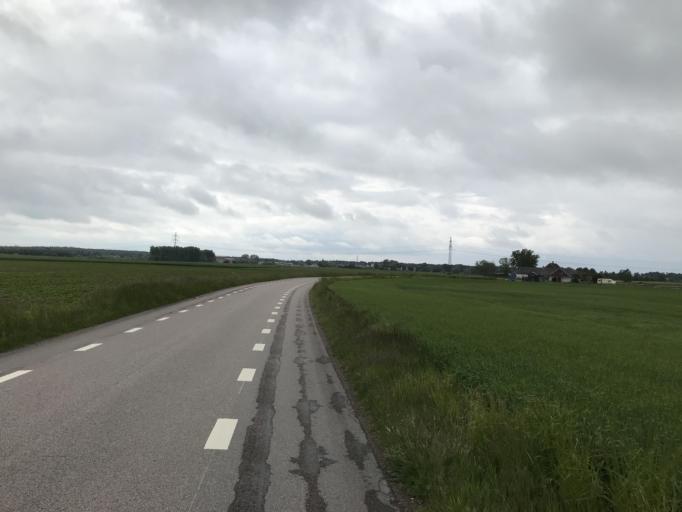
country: SE
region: Skane
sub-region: Landskrona
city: Asmundtorp
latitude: 55.8663
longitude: 12.9260
